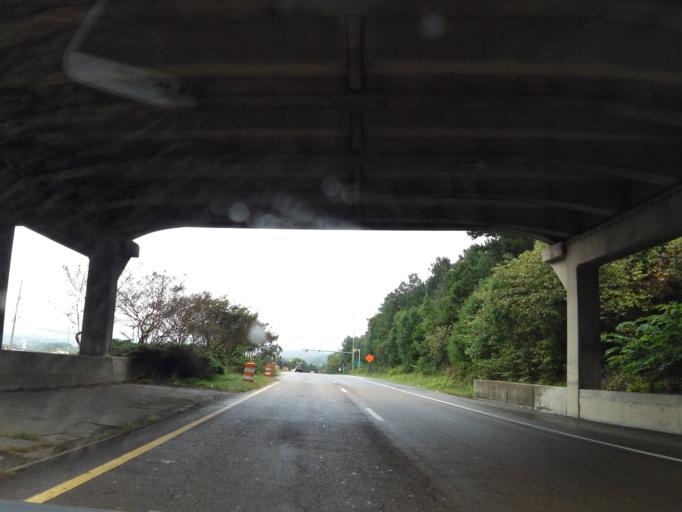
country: US
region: Tennessee
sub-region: Bradley County
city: Cleveland
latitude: 35.1941
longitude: -84.8868
